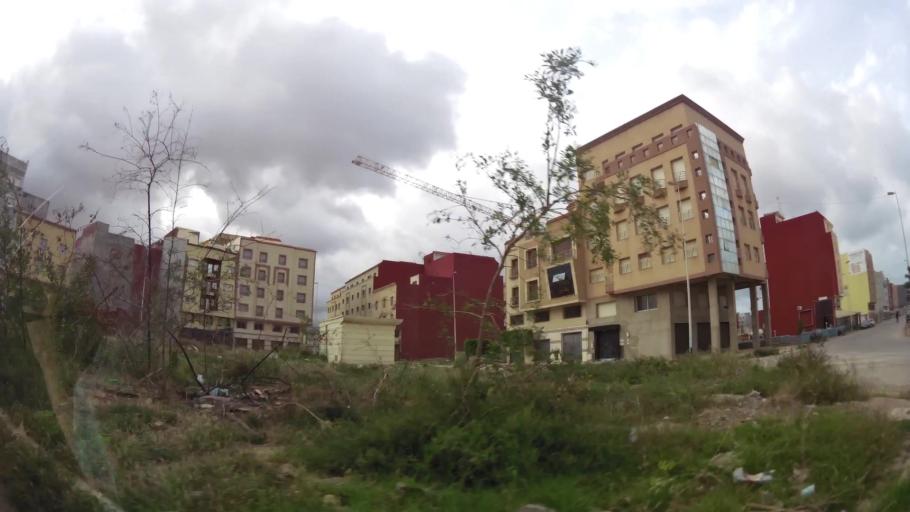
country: MA
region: Oriental
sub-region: Nador
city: Nador
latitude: 35.1532
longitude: -2.9247
